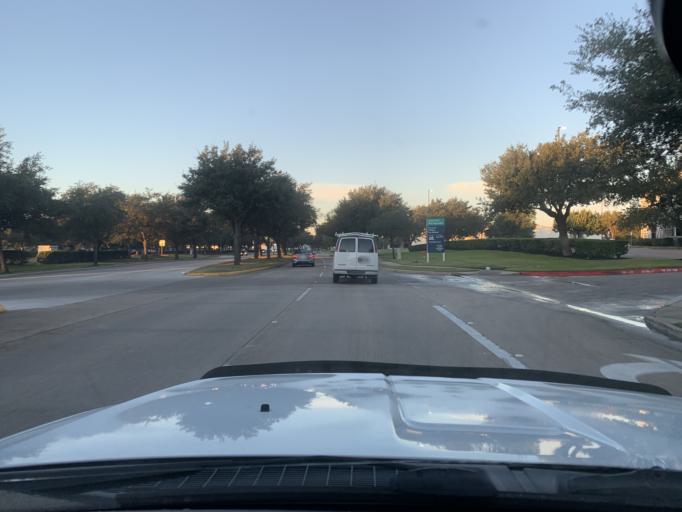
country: US
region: Texas
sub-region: Fort Bend County
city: Meadows Place
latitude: 29.6471
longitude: -95.6034
